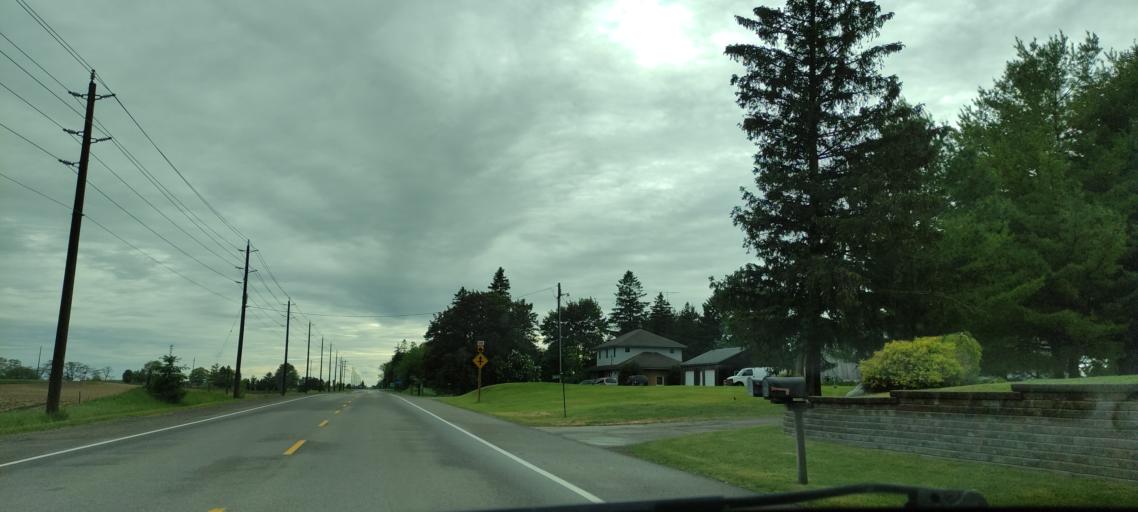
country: CA
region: Ontario
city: Kitchener
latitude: 43.3842
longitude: -80.6376
